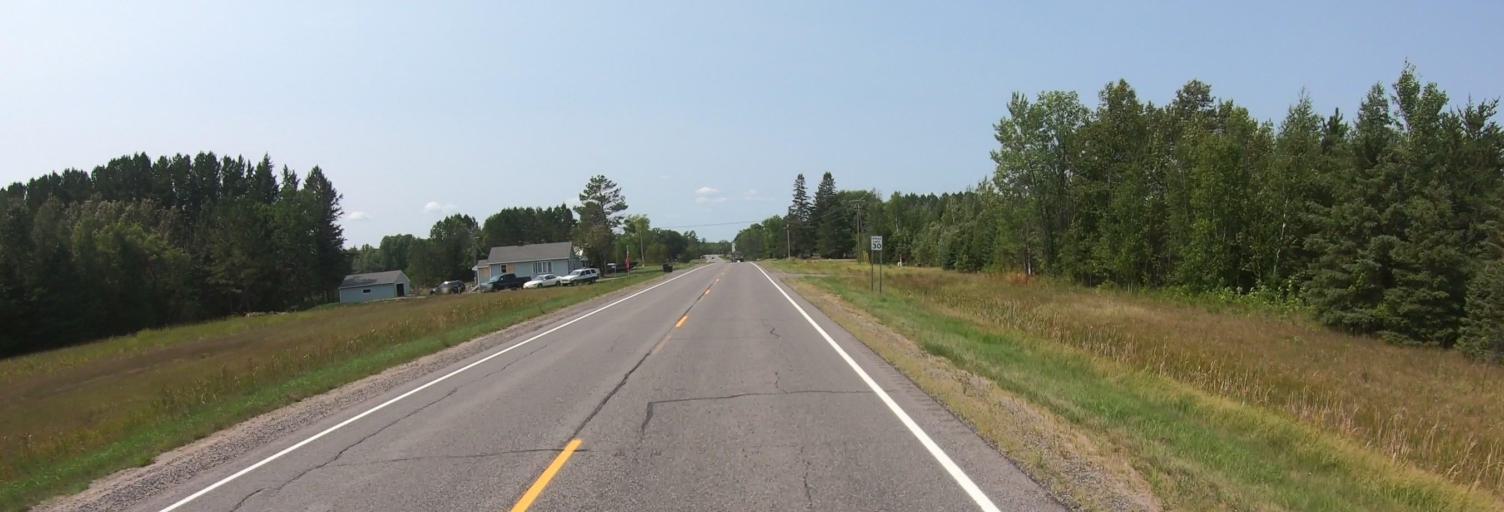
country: US
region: Minnesota
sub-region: Koochiching County
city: International Falls
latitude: 48.5129
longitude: -93.7946
